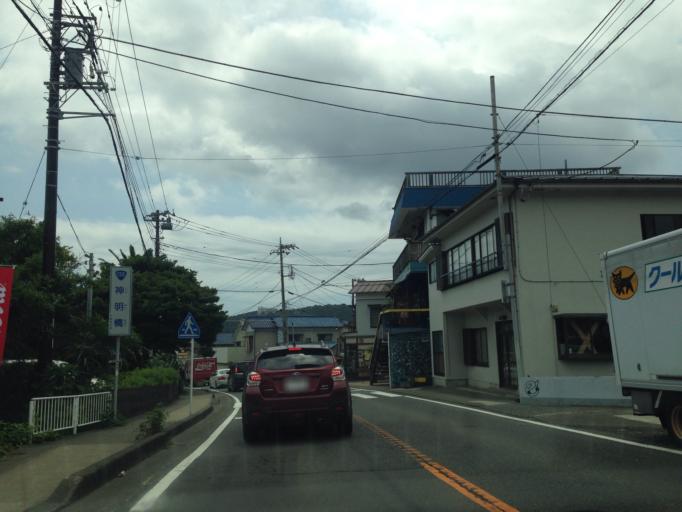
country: JP
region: Shizuoka
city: Shimoda
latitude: 34.6962
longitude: 138.9716
